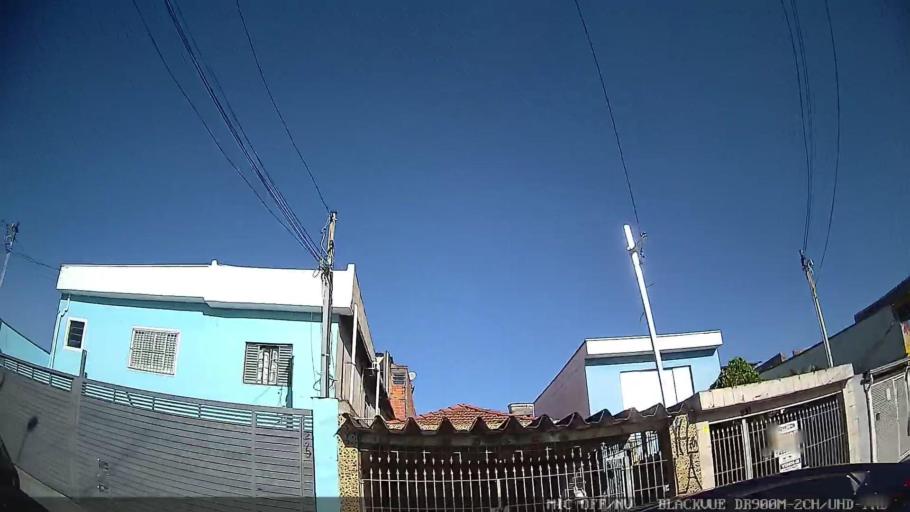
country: BR
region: Sao Paulo
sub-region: Sao Caetano Do Sul
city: Sao Caetano do Sul
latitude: -23.5462
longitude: -46.5215
